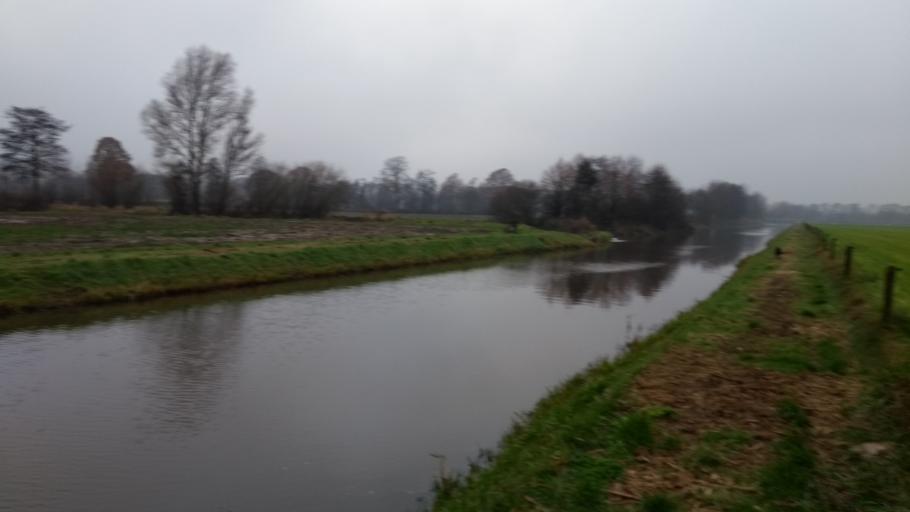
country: NL
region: Overijssel
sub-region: Gemeente Borne
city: Borne
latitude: 52.3414
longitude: 6.7327
